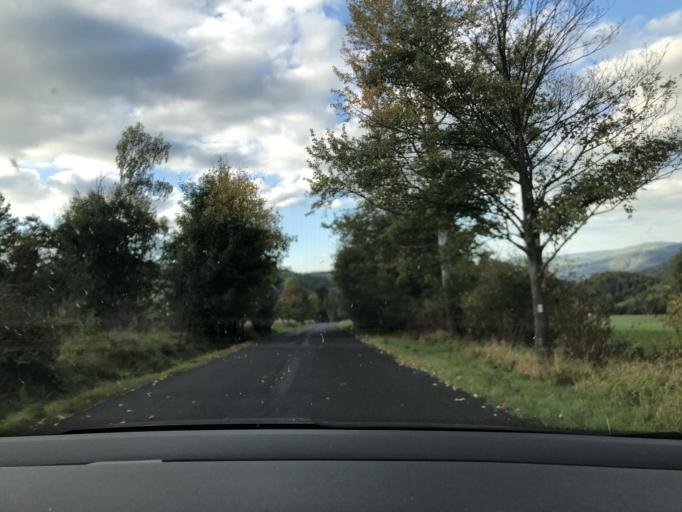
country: CZ
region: Ustecky
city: Velke Brezno
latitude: 50.6225
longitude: 14.1603
